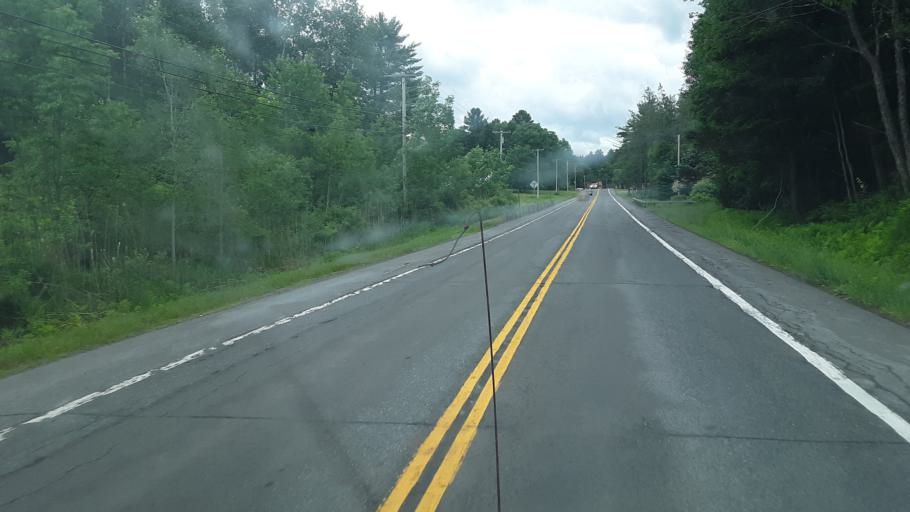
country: US
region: New York
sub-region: Oneida County
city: Rome
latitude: 43.3615
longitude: -75.4790
